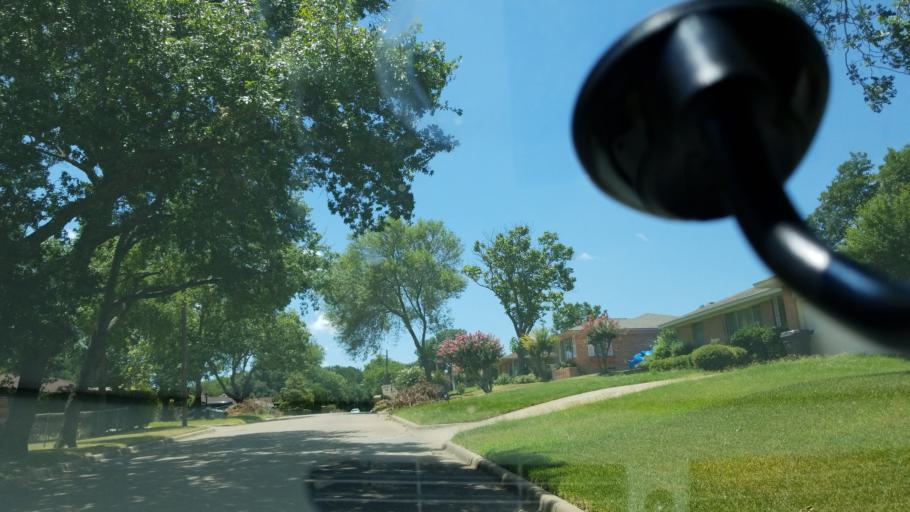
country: US
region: Texas
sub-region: Dallas County
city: Cockrell Hill
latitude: 32.6797
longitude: -96.8171
